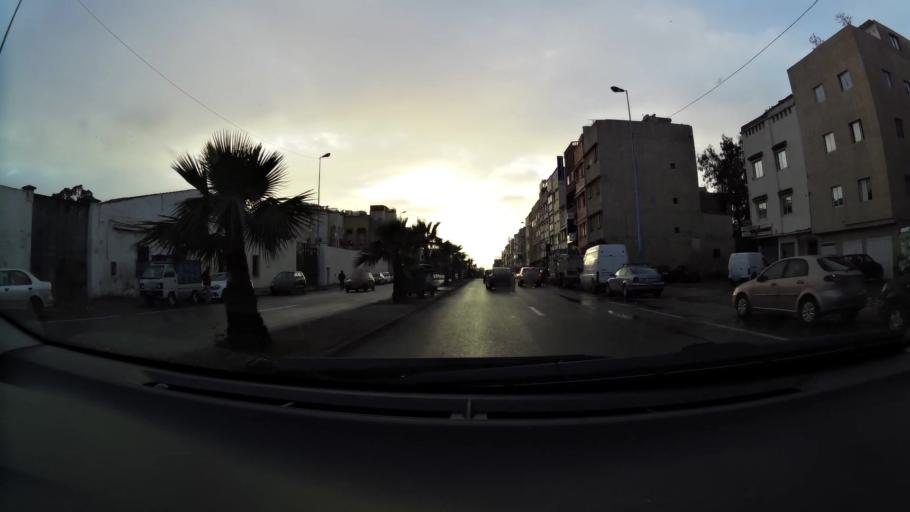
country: MA
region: Grand Casablanca
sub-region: Casablanca
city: Casablanca
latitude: 33.5826
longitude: -7.5679
